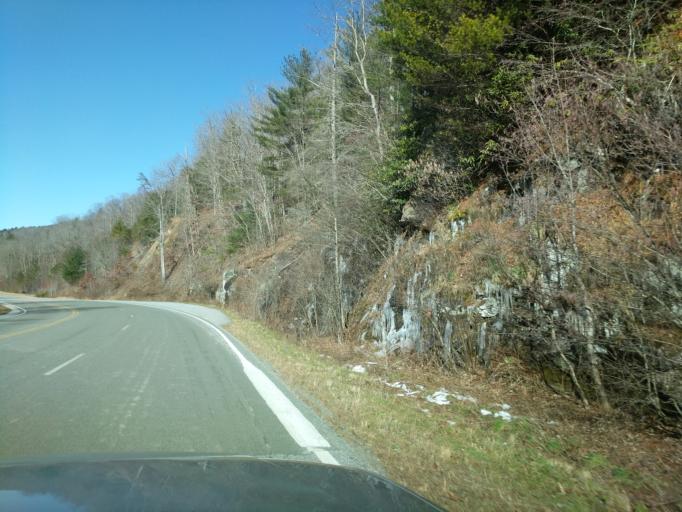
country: US
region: Georgia
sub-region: Towns County
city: Hiawassee
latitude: 34.8987
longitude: -83.6076
